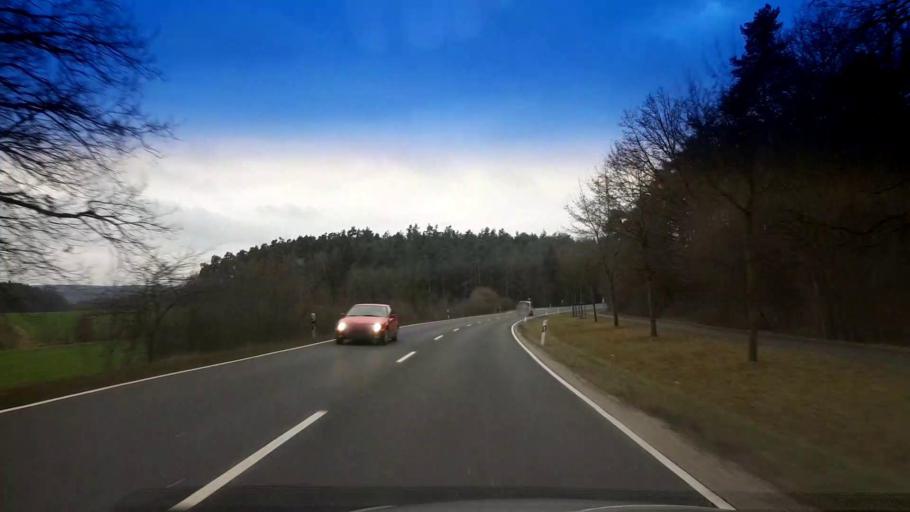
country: DE
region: Bavaria
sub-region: Upper Franconia
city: Stegaurach
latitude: 49.8375
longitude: 10.8180
